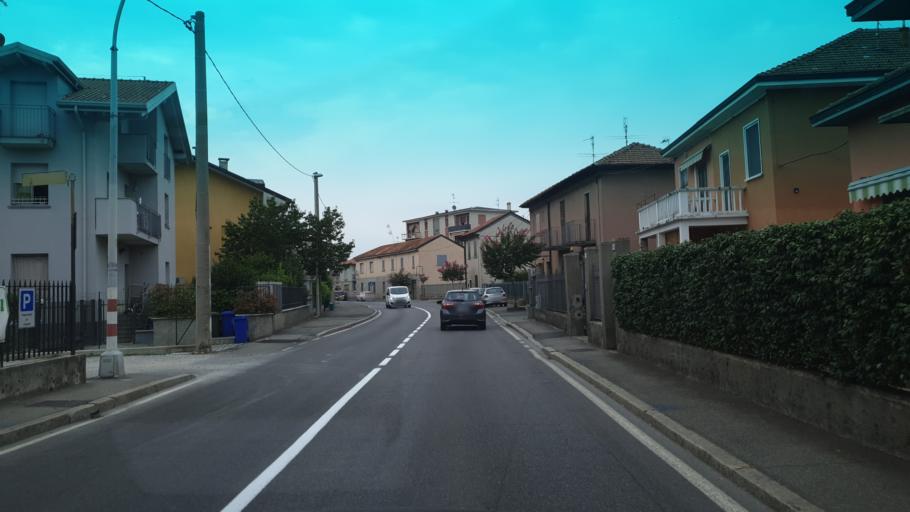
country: IT
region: Lombardy
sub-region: Provincia di Bergamo
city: Fara Gera d'Adda
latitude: 45.5525
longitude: 9.5350
